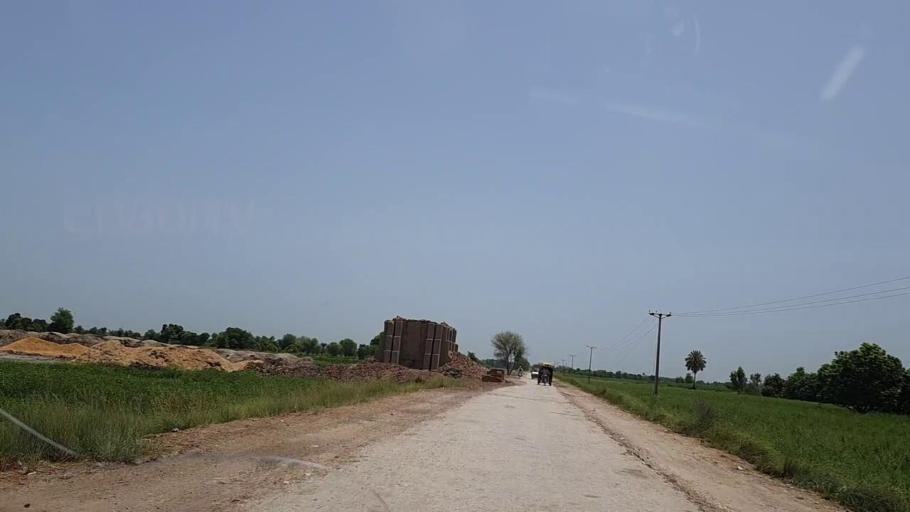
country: PK
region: Sindh
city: Tharu Shah
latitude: 26.9525
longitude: 68.0881
